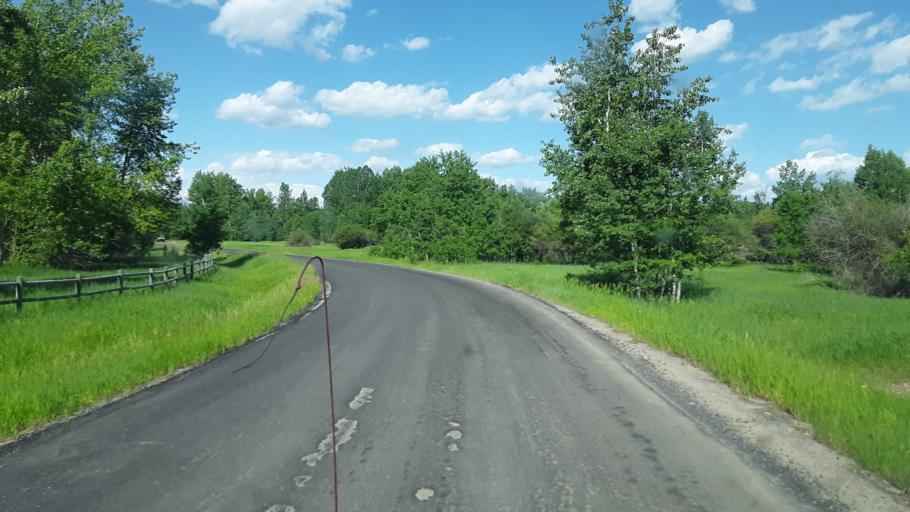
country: US
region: Montana
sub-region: Carbon County
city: Red Lodge
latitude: 45.2773
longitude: -109.2114
